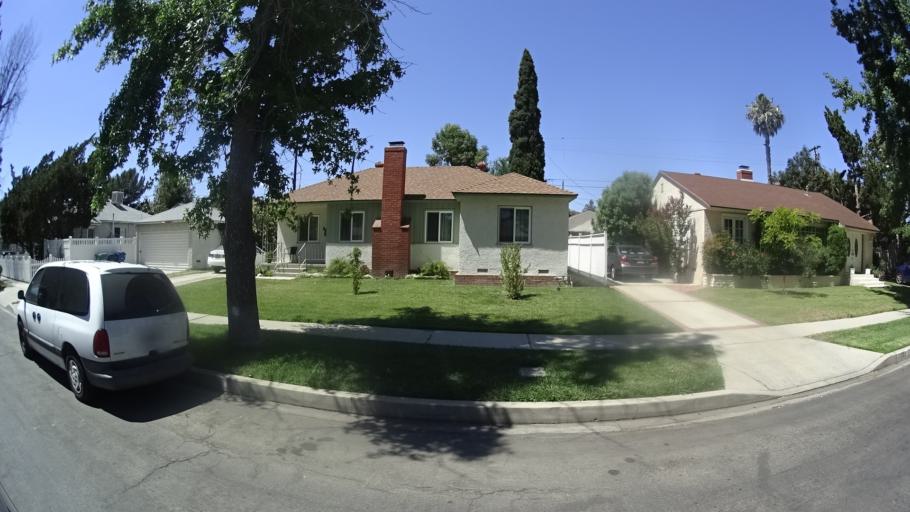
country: US
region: California
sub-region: Los Angeles County
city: Van Nuys
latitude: 34.1858
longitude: -118.4723
